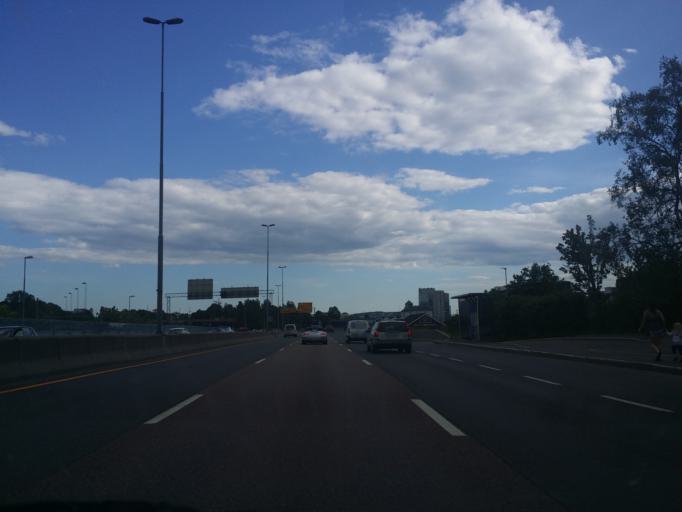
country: NO
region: Oslo
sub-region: Oslo
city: Oslo
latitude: 59.9411
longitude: 10.7810
